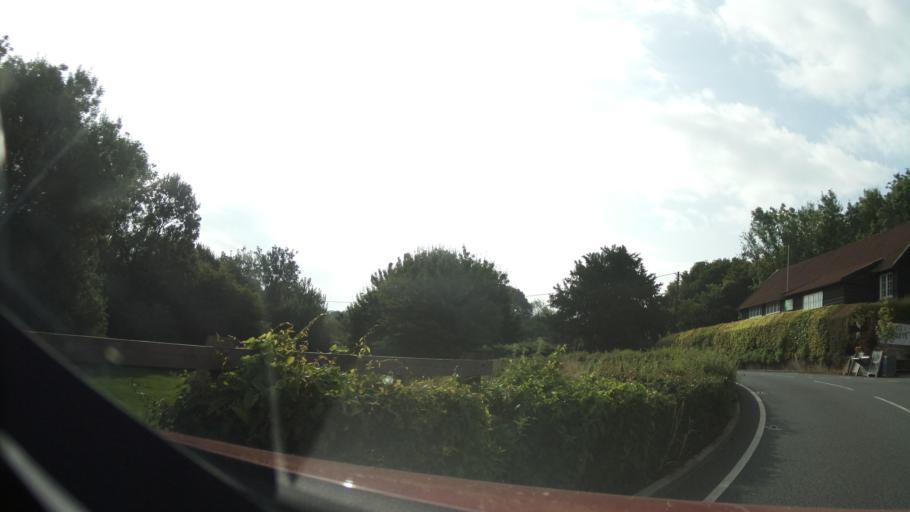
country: GB
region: England
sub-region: North Somerset
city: Long Ashton
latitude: 51.4082
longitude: -2.6761
